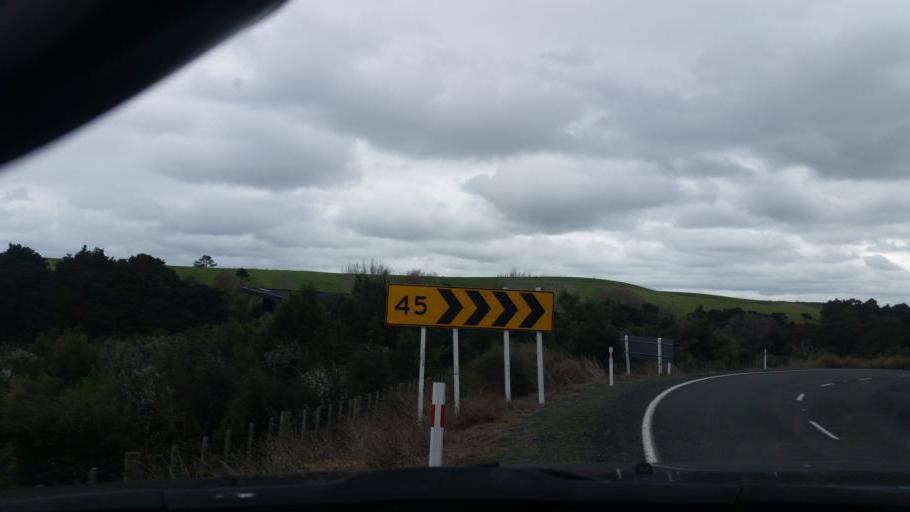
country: NZ
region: Northland
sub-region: Whangarei
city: Ruakaka
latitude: -36.0729
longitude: 174.5761
